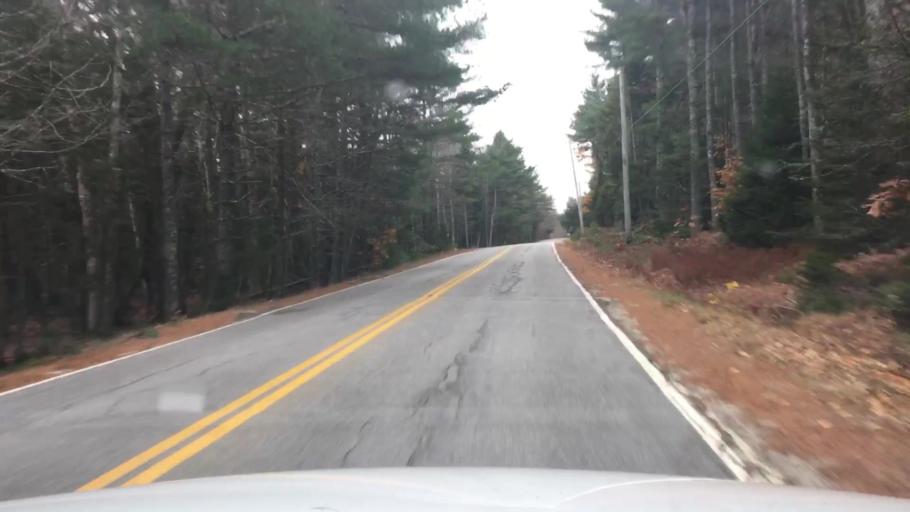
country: US
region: Maine
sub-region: Hancock County
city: Sedgwick
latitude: 44.3214
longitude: -68.5707
